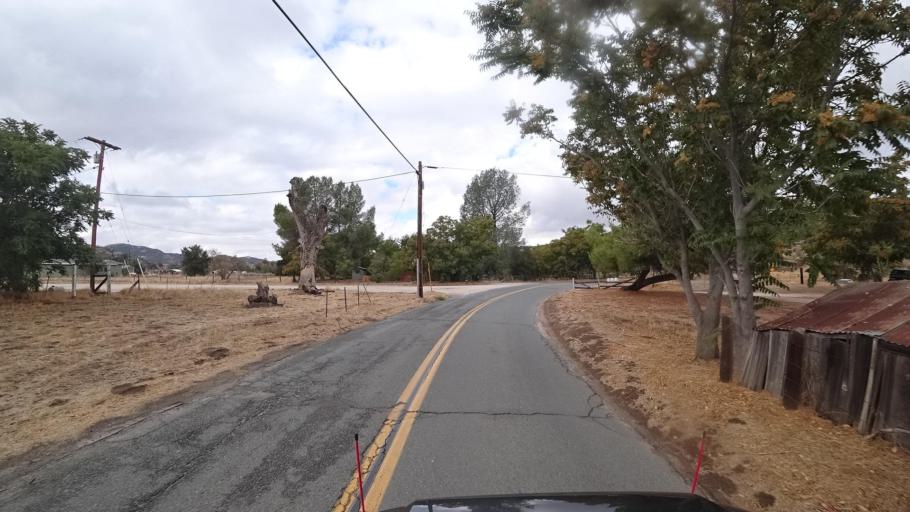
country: US
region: California
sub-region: San Diego County
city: Campo
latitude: 32.6311
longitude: -116.4320
